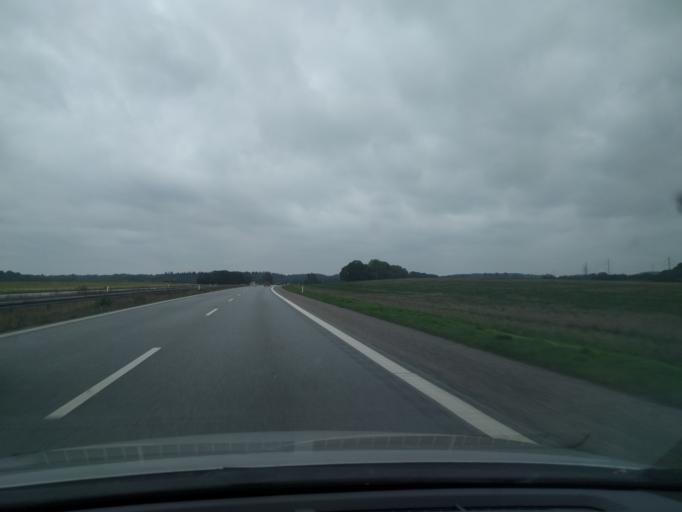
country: DK
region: Zealand
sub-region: Ringsted Kommune
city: Ringsted
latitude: 55.4568
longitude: 11.8797
